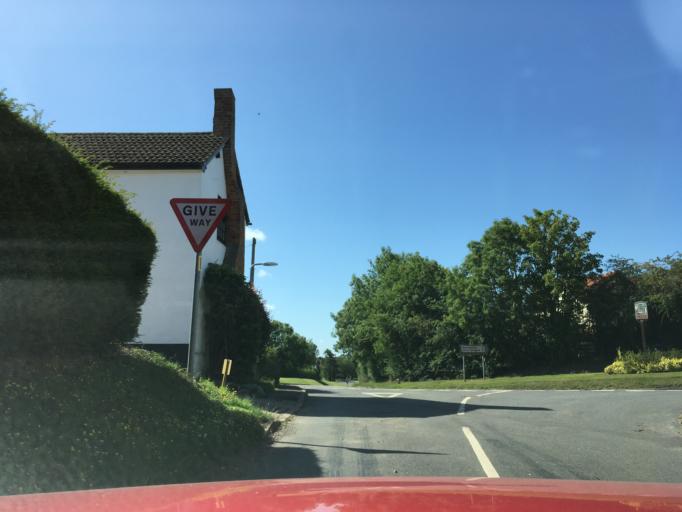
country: GB
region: England
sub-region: Milton Keynes
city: Calverton
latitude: 51.9995
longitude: -0.8613
